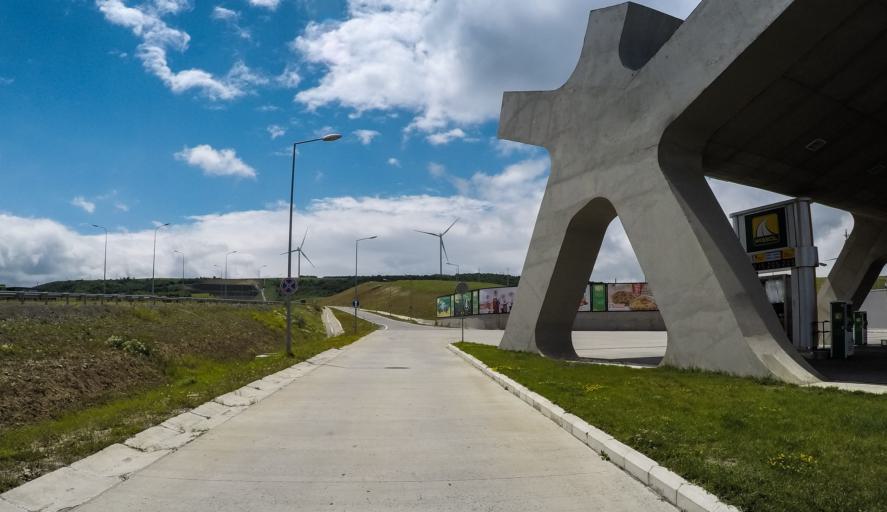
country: GE
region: Shida Kartli
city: Gori
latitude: 42.0157
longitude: 44.0643
